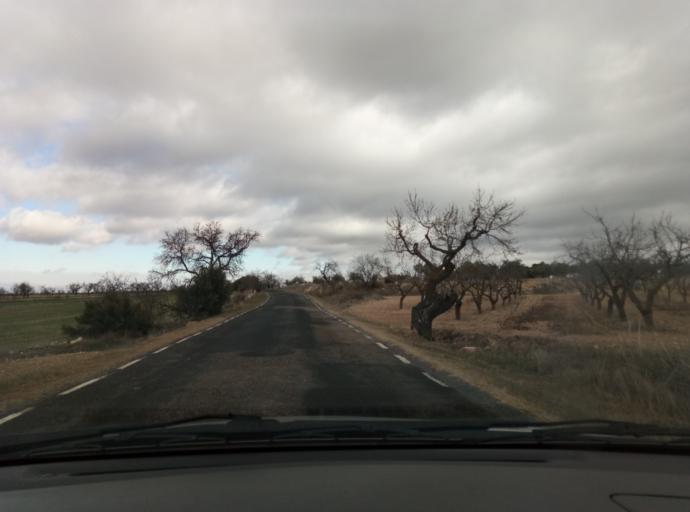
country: ES
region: Catalonia
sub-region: Provincia de Lleida
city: Nalec
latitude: 41.5759
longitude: 1.0752
